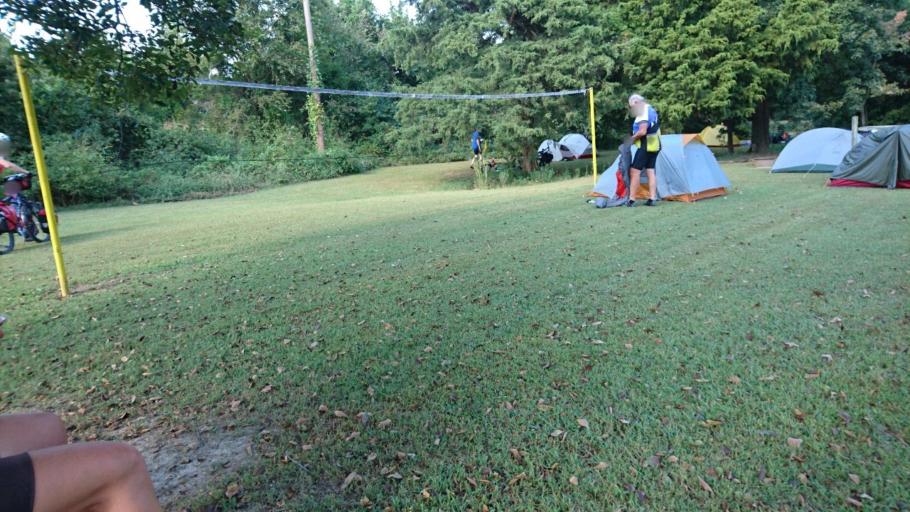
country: US
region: Missouri
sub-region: Laclede County
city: Lebanon
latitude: 37.6022
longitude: -92.7092
